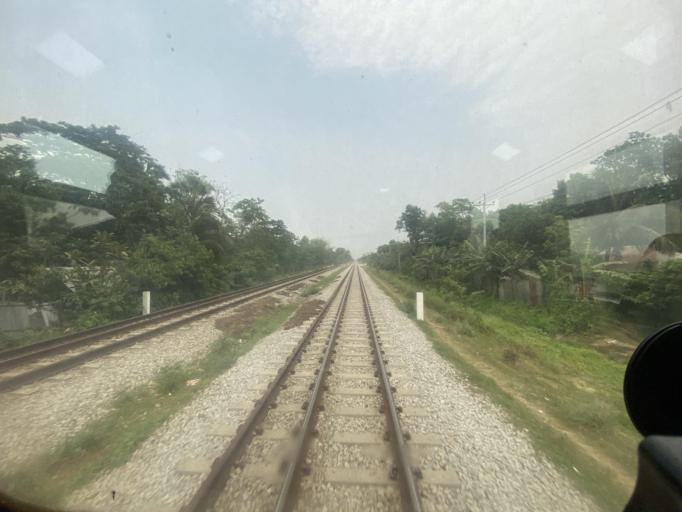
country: BD
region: Chittagong
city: Laksham
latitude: 23.3185
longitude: 91.1417
